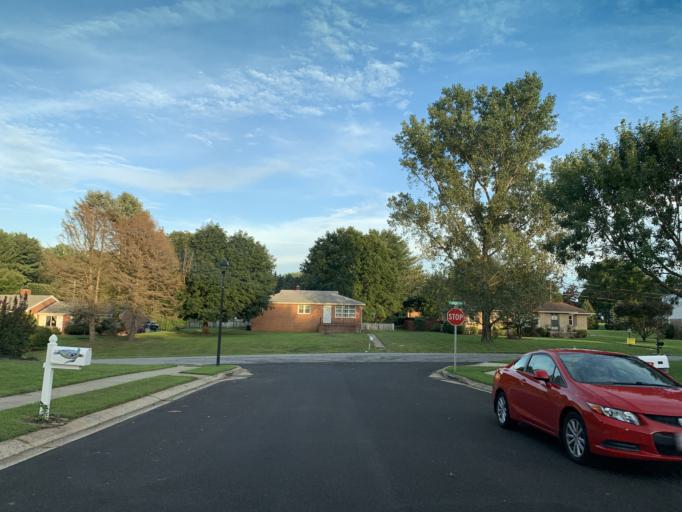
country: US
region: Maryland
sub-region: Harford County
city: Aberdeen
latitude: 39.5215
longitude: -76.1596
